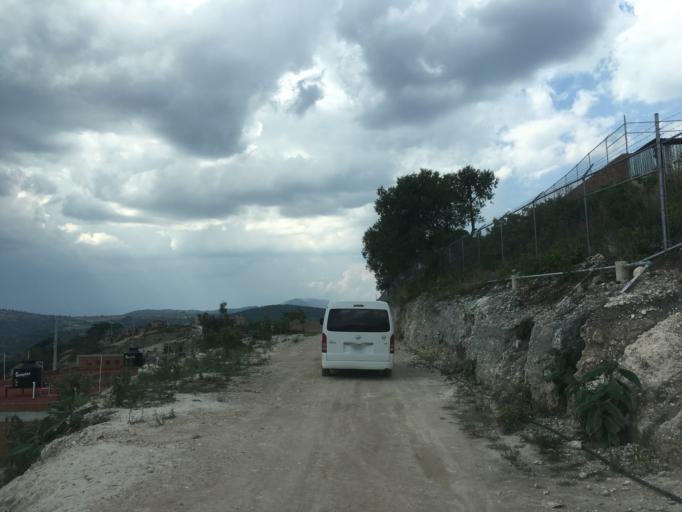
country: MX
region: Oaxaca
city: Santiago Tilantongo
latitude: 17.2215
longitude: -97.2717
